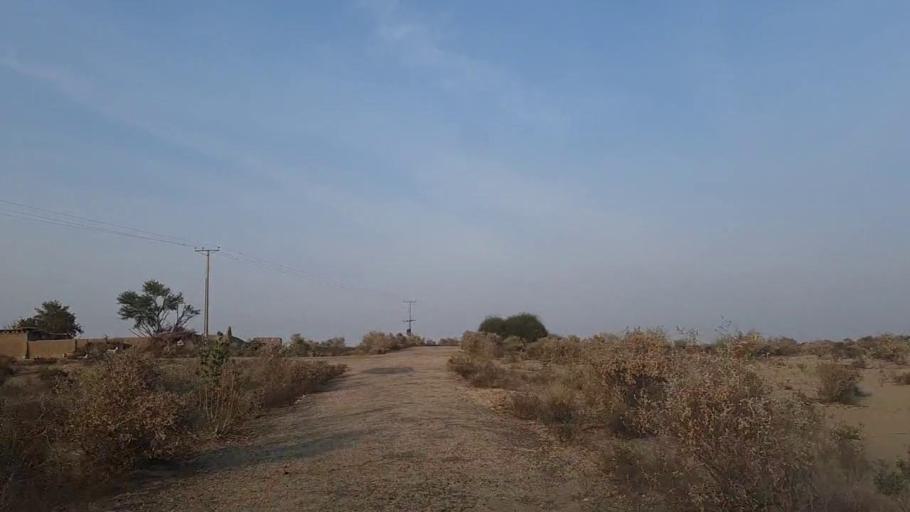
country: PK
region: Sindh
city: Jam Sahib
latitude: 26.4336
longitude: 68.6038
